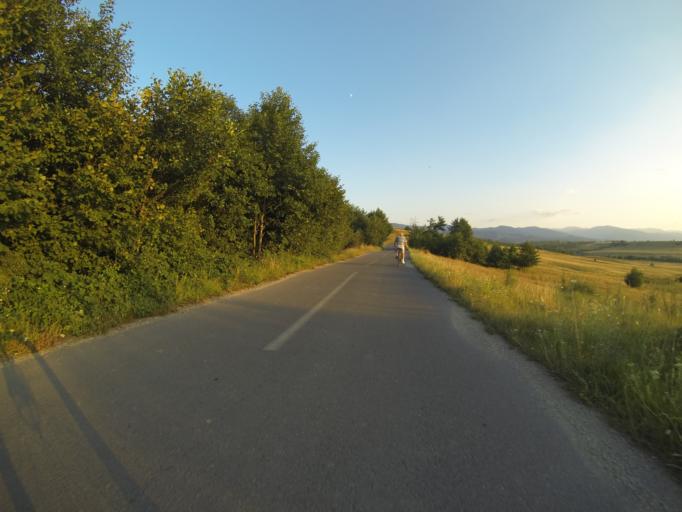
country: RO
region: Brasov
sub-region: Comuna Sinca Veche
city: Sinca Veche
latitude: 45.7509
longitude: 25.1650
